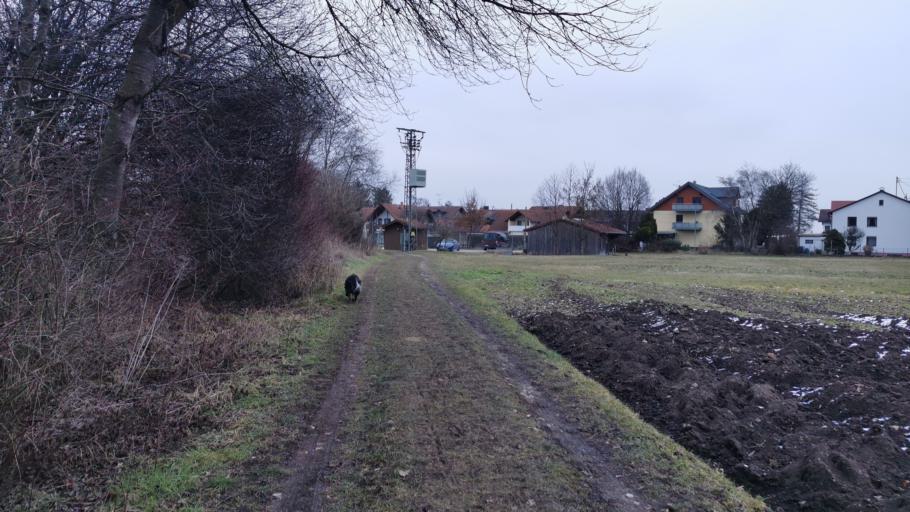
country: DE
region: Bavaria
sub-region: Upper Bavaria
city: Kirchheim bei Muenchen
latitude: 48.1984
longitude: 11.7689
